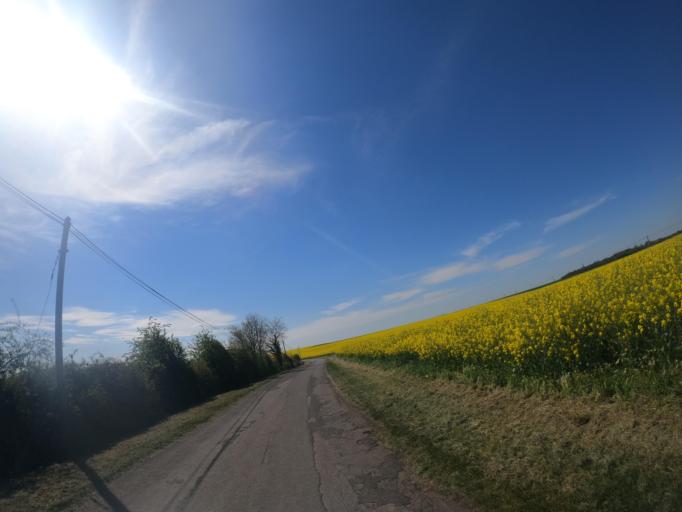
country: FR
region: Poitou-Charentes
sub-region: Departement des Deux-Sevres
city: Airvault
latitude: 46.8856
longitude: -0.1504
